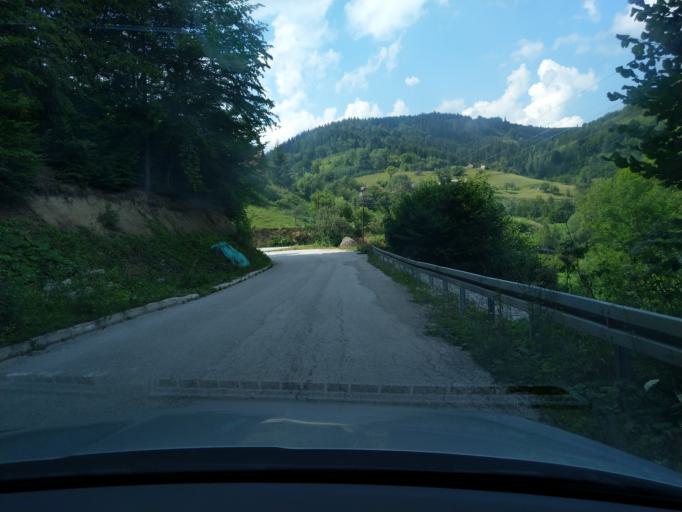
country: RS
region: Central Serbia
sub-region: Zlatiborski Okrug
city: Nova Varos
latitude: 43.5828
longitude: 19.8785
